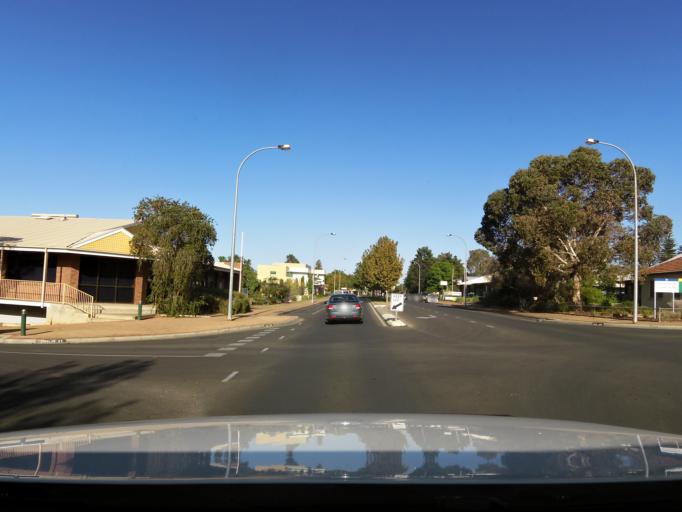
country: AU
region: South Australia
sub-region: Berri and Barmera
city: Berri
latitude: -34.2838
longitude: 140.6041
